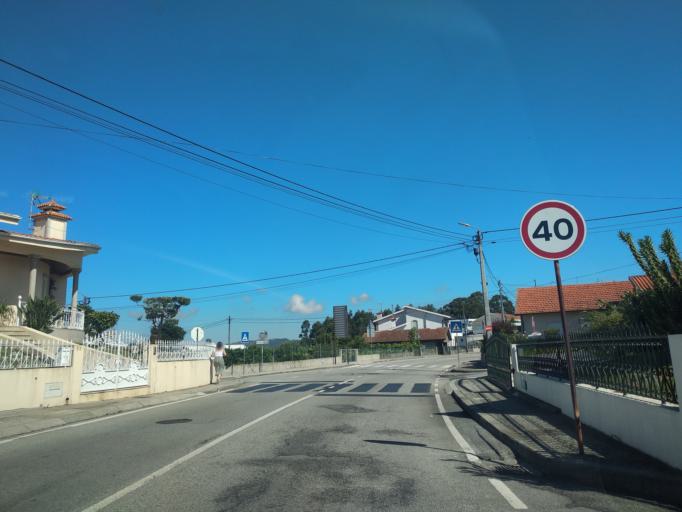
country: PT
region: Porto
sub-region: Pacos de Ferreira
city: Ferreira
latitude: 41.2697
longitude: -8.3363
